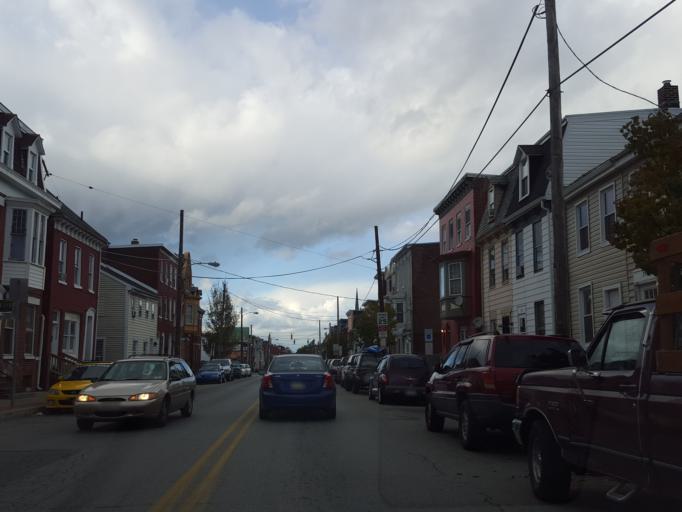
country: US
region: Pennsylvania
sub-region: York County
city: York
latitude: 39.9599
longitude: -76.7219
